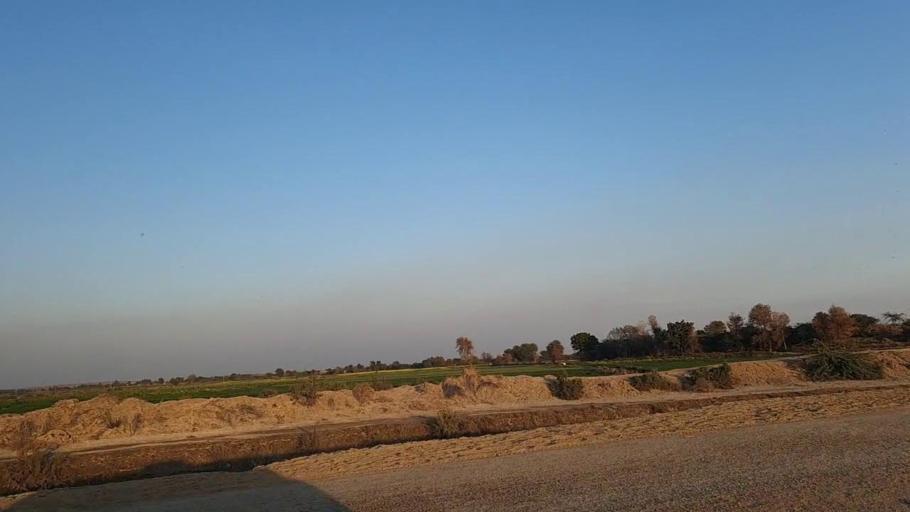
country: PK
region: Sindh
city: Jam Sahib
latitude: 26.3258
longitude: 68.6297
